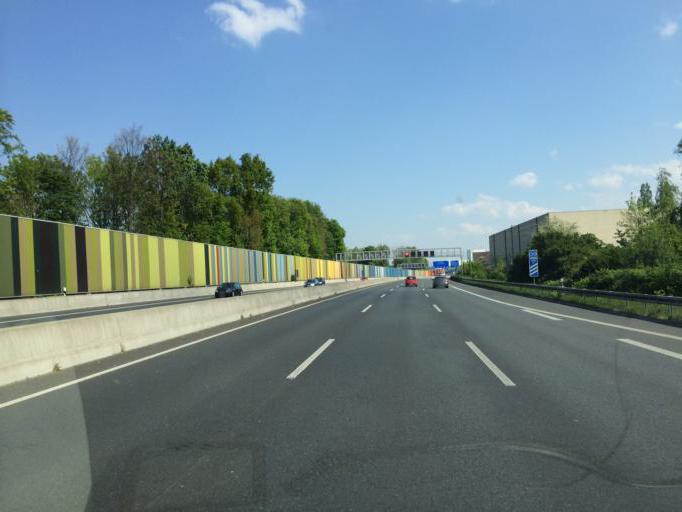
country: DE
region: North Rhine-Westphalia
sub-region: Regierungsbezirk Munster
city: Gelsenkirchen
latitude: 51.4743
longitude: 7.1288
